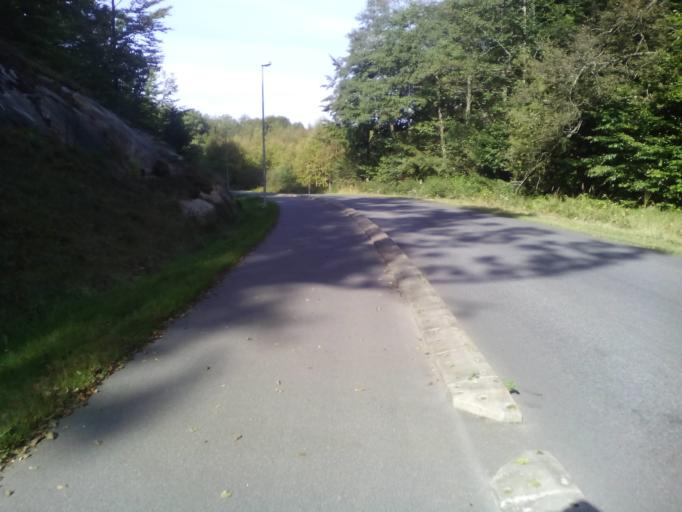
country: SE
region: Blekinge
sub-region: Karlshamns Kommun
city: Karlshamn
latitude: 56.1668
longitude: 14.8968
